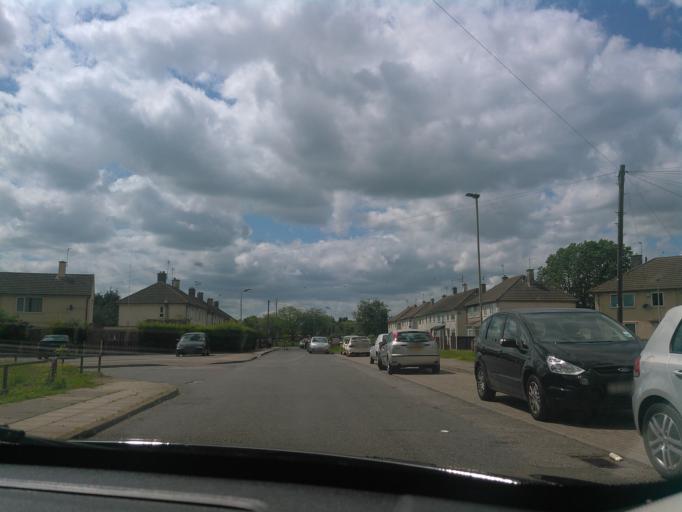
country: GB
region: England
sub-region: Leicestershire
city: Glenfield
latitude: 52.6383
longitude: -1.1904
